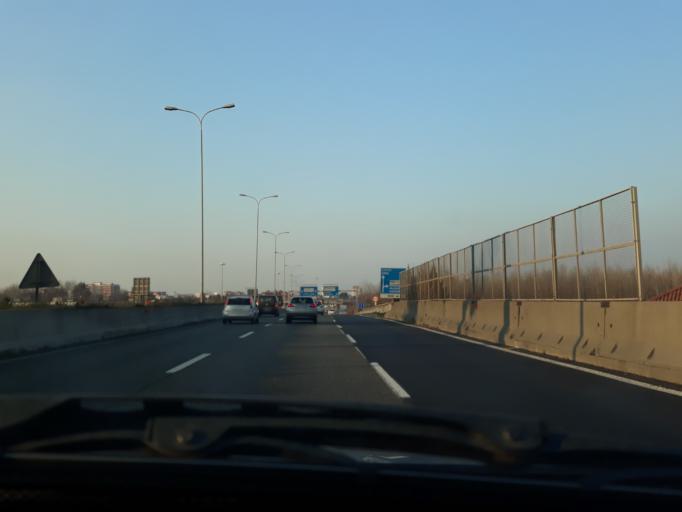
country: IT
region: Lombardy
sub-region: Provincia di Monza e Brianza
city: Muggio
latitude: 45.5911
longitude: 9.2461
